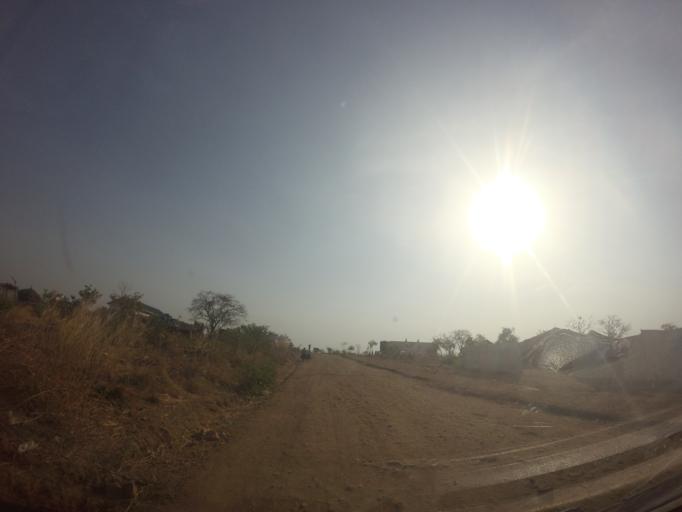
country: UG
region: Northern Region
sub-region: Maracha District
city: Maracha
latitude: 3.1205
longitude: 31.1583
